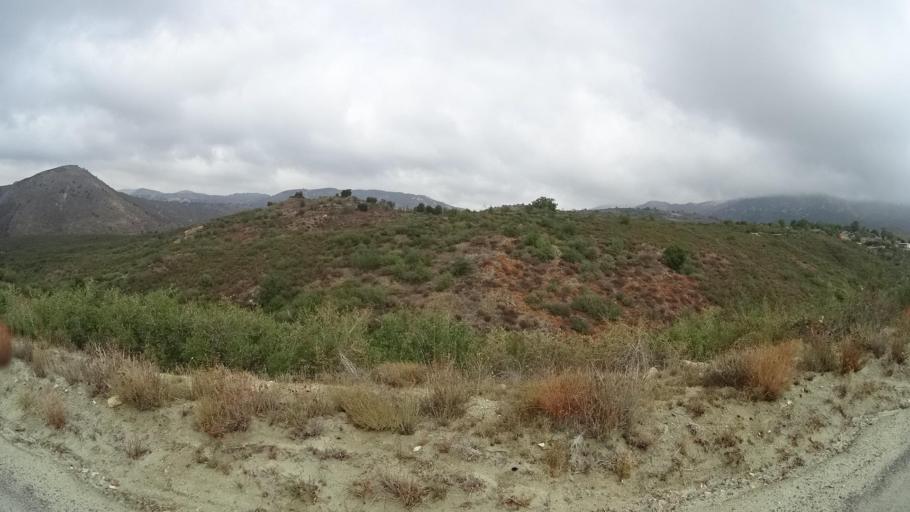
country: US
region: California
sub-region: San Diego County
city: Descanso
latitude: 32.9579
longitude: -116.6503
